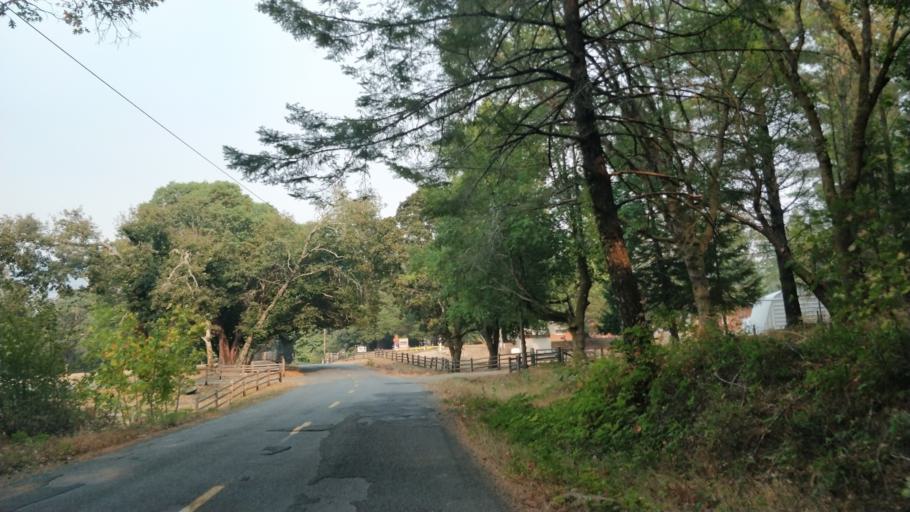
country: US
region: California
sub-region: Humboldt County
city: Rio Dell
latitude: 40.2375
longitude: -124.1340
